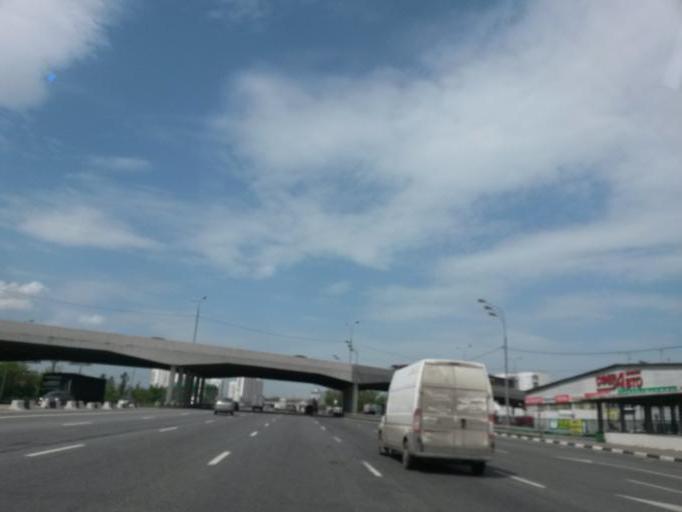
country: RU
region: Moscow
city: Annino
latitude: 55.5741
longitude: 37.5975
